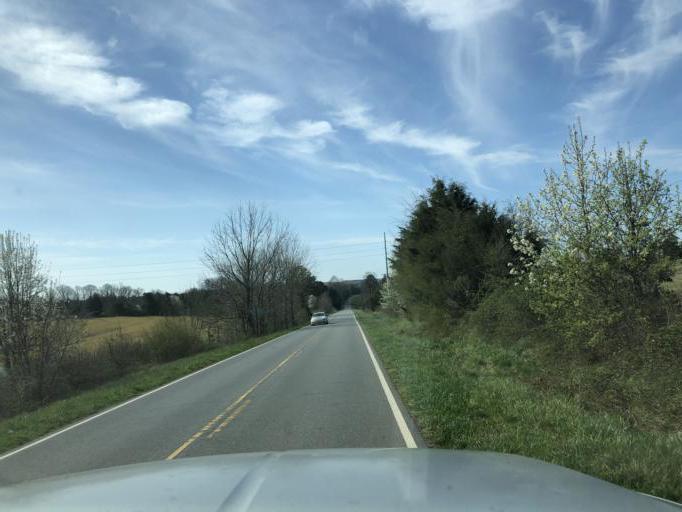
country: US
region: North Carolina
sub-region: Cleveland County
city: Shelby
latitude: 35.4660
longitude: -81.6341
